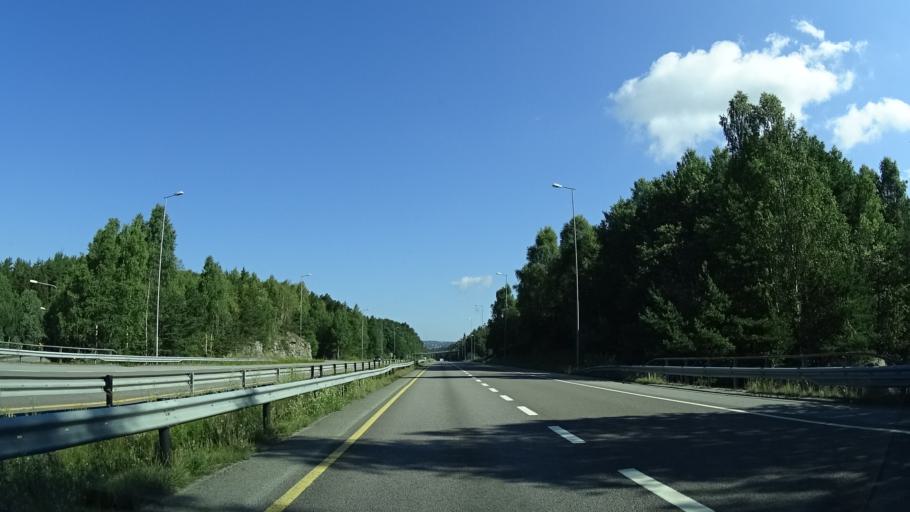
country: NO
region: Akershus
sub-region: Oppegard
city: Kolbotn
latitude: 59.8236
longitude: 10.7763
